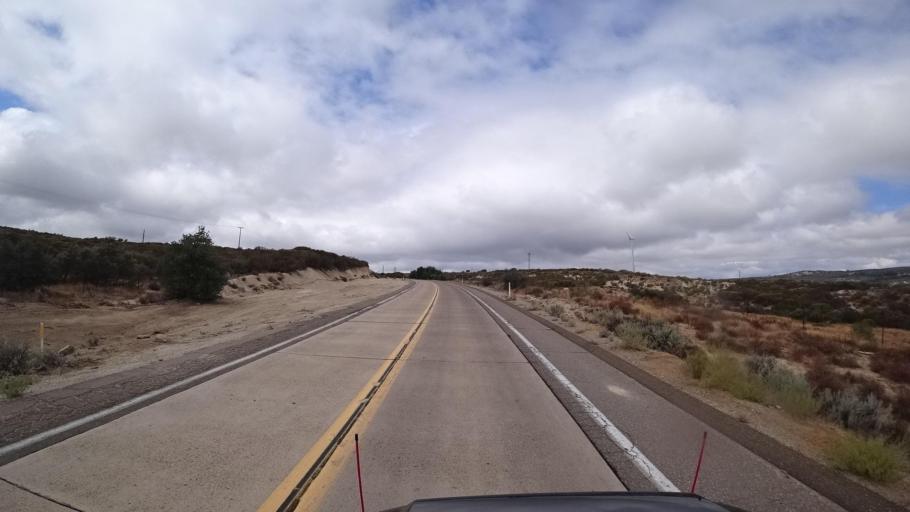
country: US
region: California
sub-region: San Diego County
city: Campo
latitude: 32.6961
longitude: -116.3471
